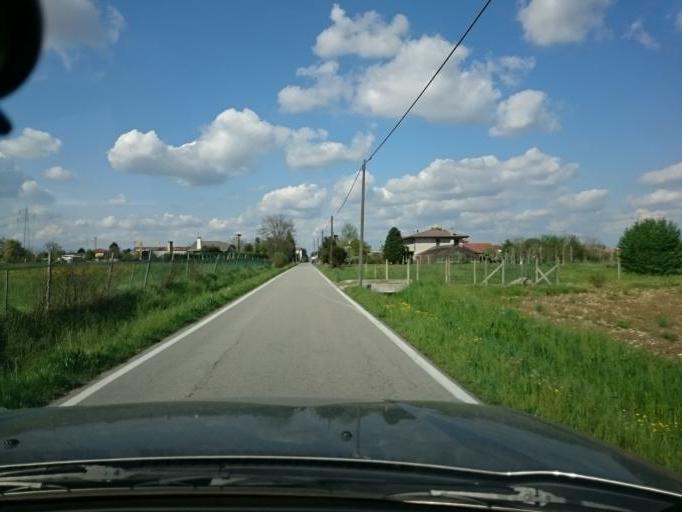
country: IT
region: Veneto
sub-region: Provincia di Padova
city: Villanova
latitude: 45.4844
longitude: 11.9848
